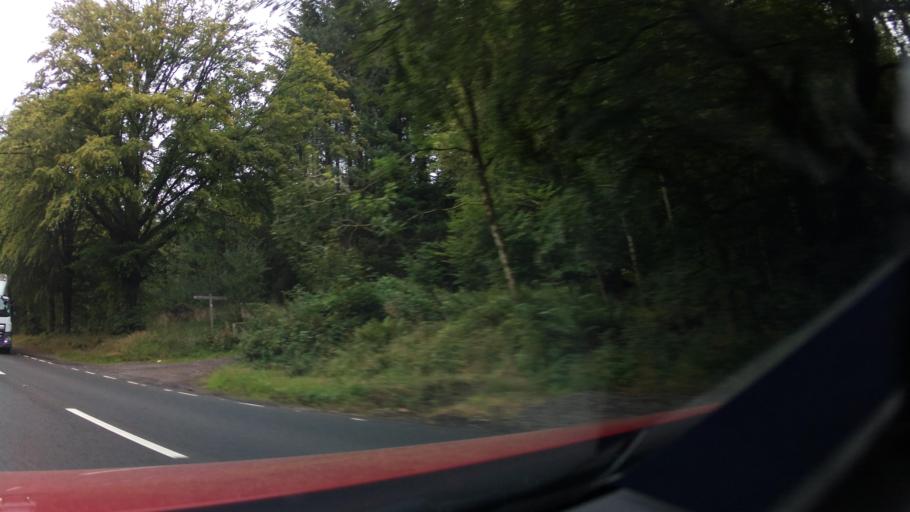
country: GB
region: Scotland
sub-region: Dumfries and Galloway
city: Moffat
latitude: 55.2421
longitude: -3.4614
